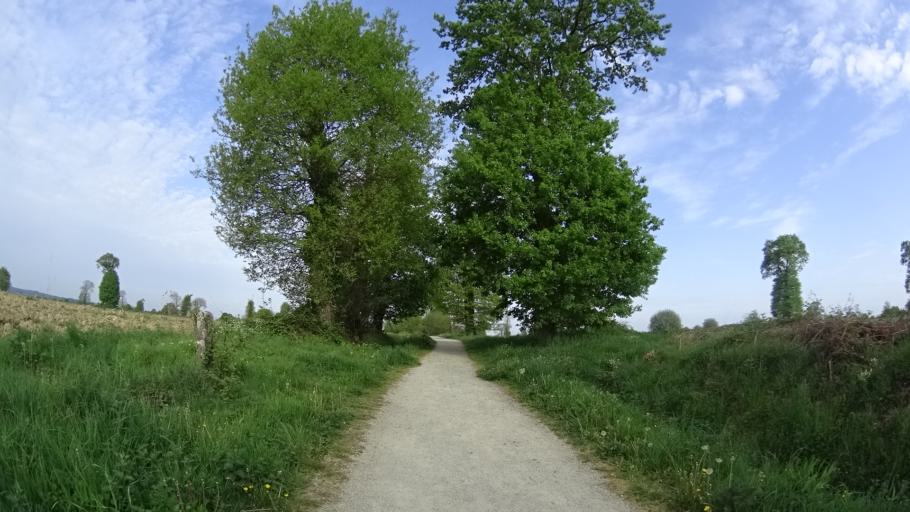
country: FR
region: Brittany
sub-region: Departement d'Ille-et-Vilaine
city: La Meziere
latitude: 48.2186
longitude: -1.7660
